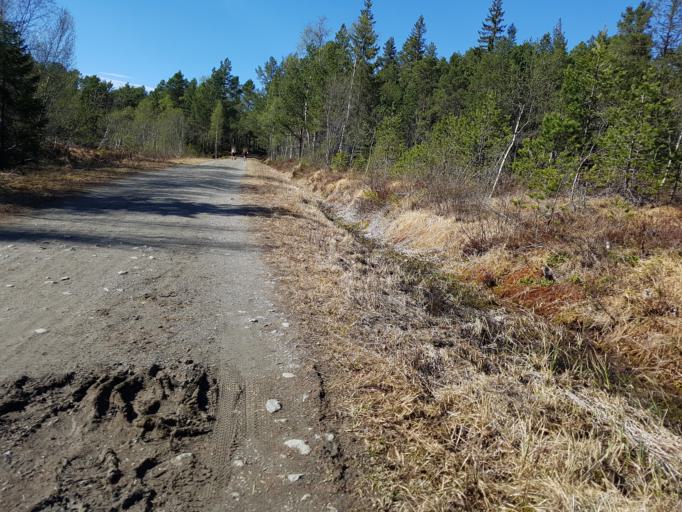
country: NO
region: Sor-Trondelag
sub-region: Trondheim
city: Trondheim
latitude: 63.4402
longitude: 10.3233
